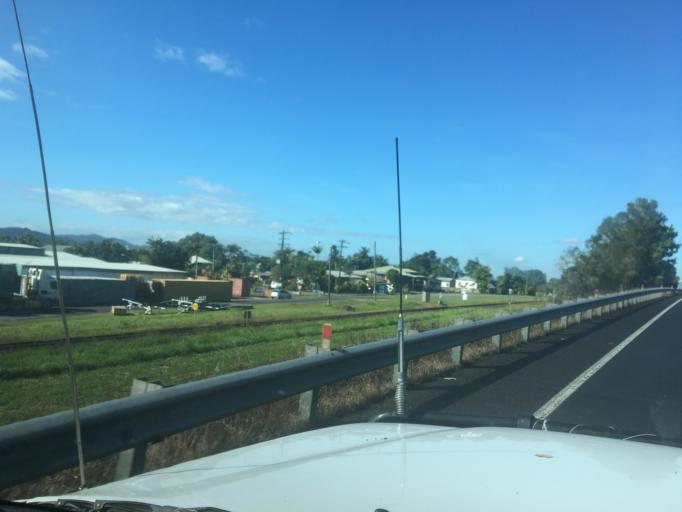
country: AU
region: Queensland
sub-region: Cassowary Coast
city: Innisfail
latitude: -17.3324
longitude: 145.9280
